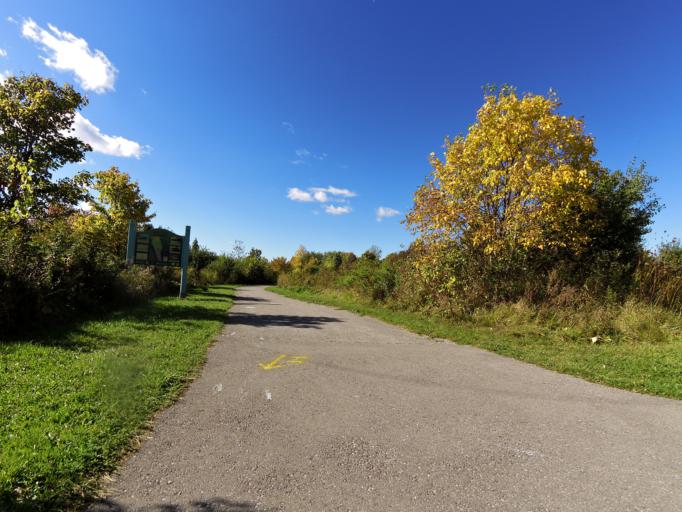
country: CA
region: Ontario
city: Ajax
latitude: 43.8491
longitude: -78.9505
